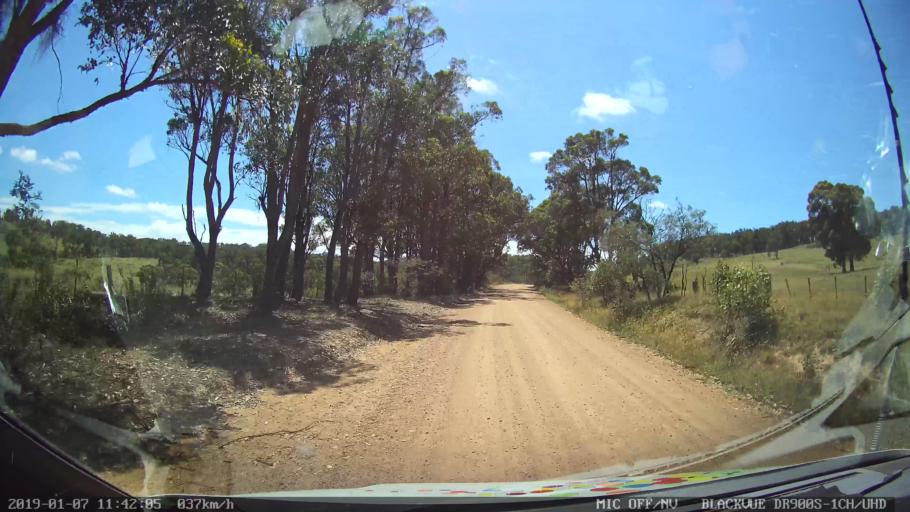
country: AU
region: New South Wales
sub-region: Guyra
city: Guyra
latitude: -30.3581
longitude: 151.5916
